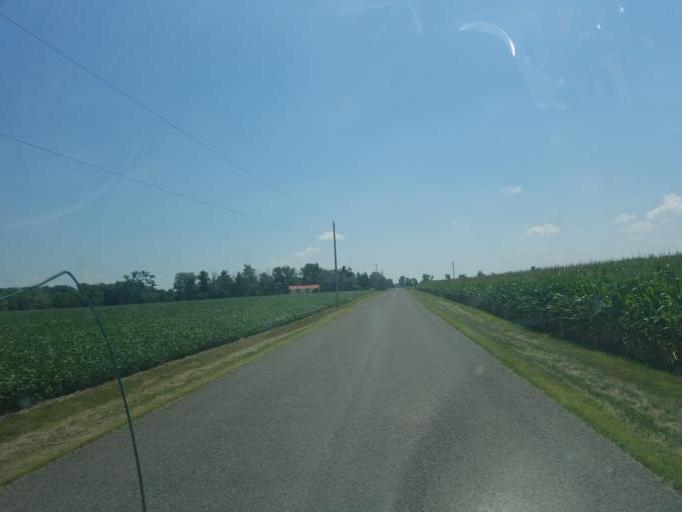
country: US
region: Ohio
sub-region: Auglaize County
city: Wapakoneta
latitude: 40.5350
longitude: -84.2311
